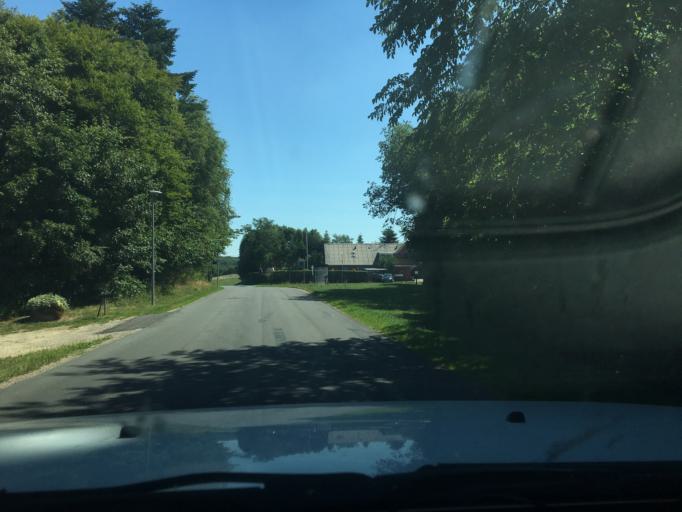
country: DK
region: Central Jutland
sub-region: Horsens Kommune
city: Braedstrup
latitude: 55.9579
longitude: 9.5905
